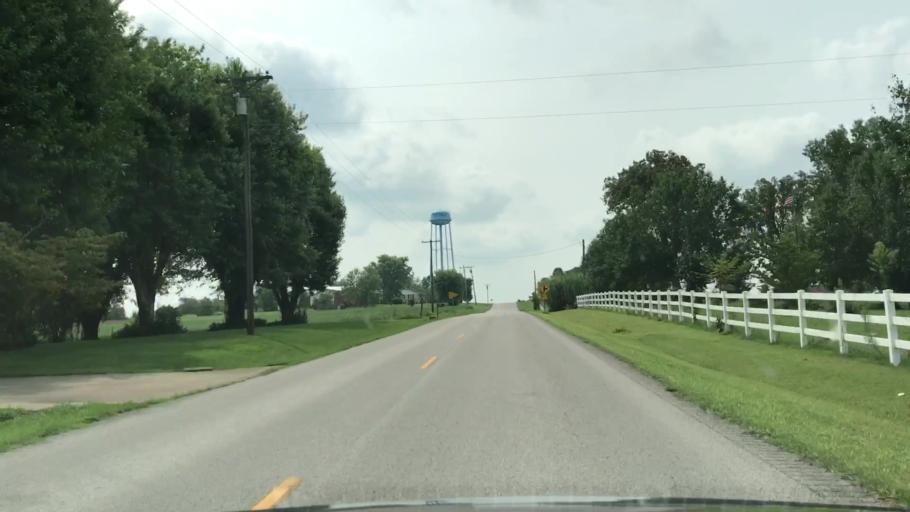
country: US
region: Kentucky
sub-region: Edmonson County
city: Brownsville
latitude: 37.1152
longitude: -86.1506
